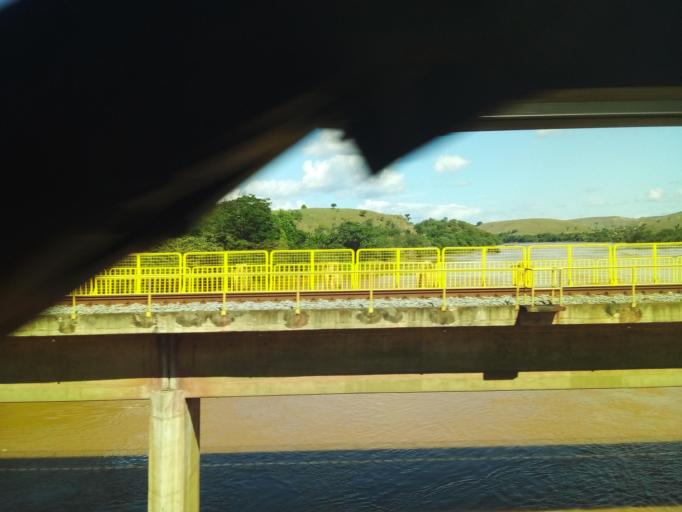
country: BR
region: Minas Gerais
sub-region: Governador Valadares
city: Governador Valadares
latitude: -18.8526
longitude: -41.8614
